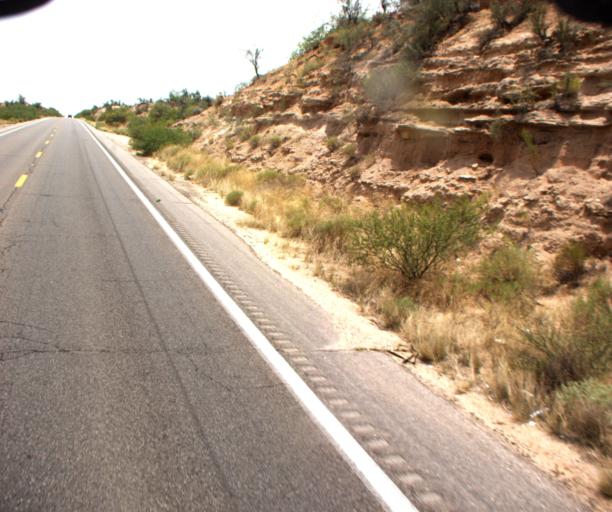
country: US
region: Arizona
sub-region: Gila County
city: San Carlos
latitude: 33.3398
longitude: -110.5984
